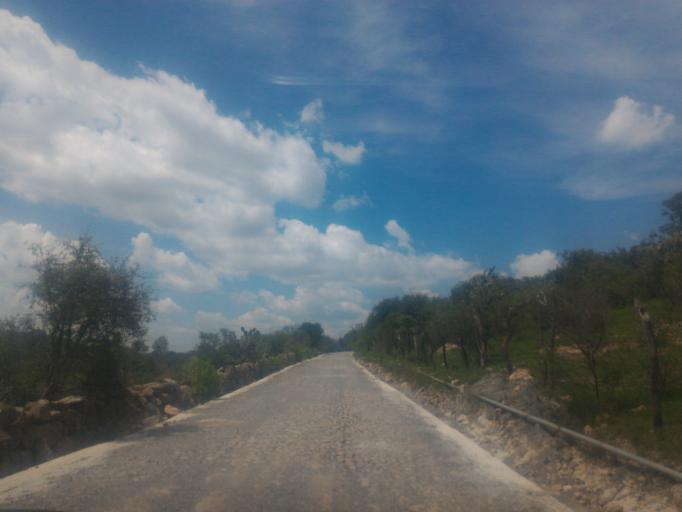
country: MX
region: Guanajuato
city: Ciudad Manuel Doblado
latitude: 20.8009
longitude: -102.0777
